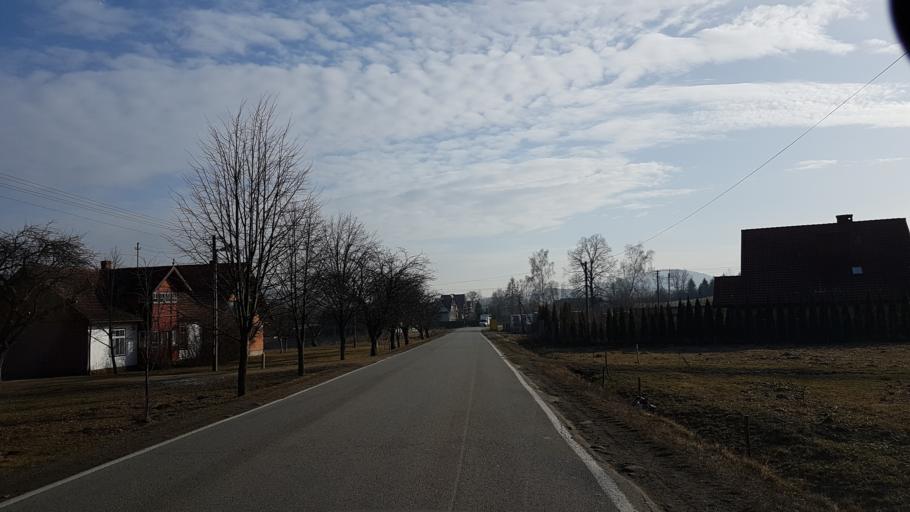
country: PL
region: Lesser Poland Voivodeship
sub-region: Powiat limanowski
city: Lukowica
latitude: 49.6518
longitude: 20.4985
